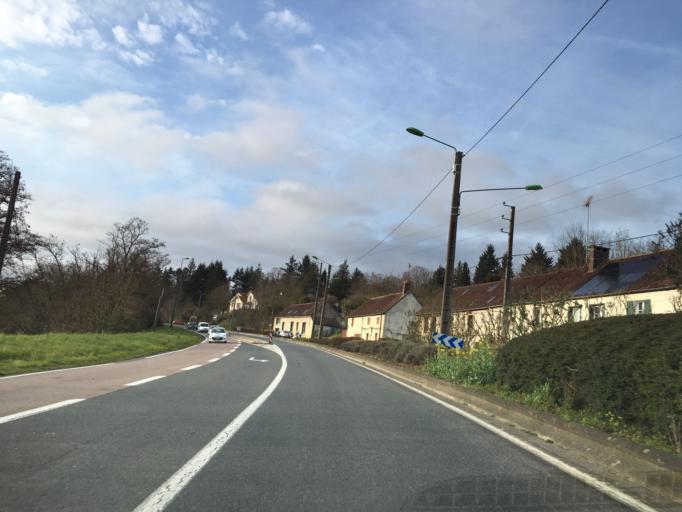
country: FR
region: Bourgogne
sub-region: Departement de l'Yonne
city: Maillot
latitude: 48.1526
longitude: 3.3095
